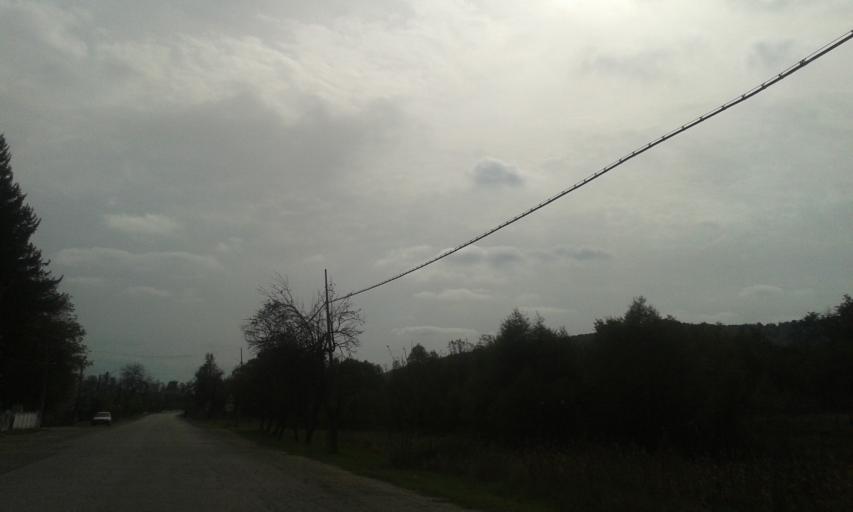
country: RO
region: Gorj
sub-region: Comuna Licuriciu
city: Licuriciu
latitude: 44.8808
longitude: 23.6316
